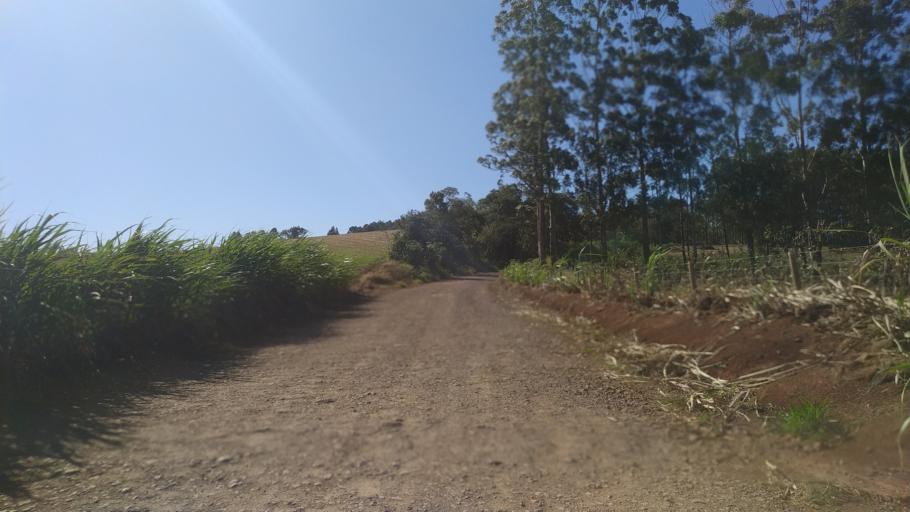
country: BR
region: Santa Catarina
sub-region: Chapeco
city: Chapeco
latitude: -27.1492
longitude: -52.6114
